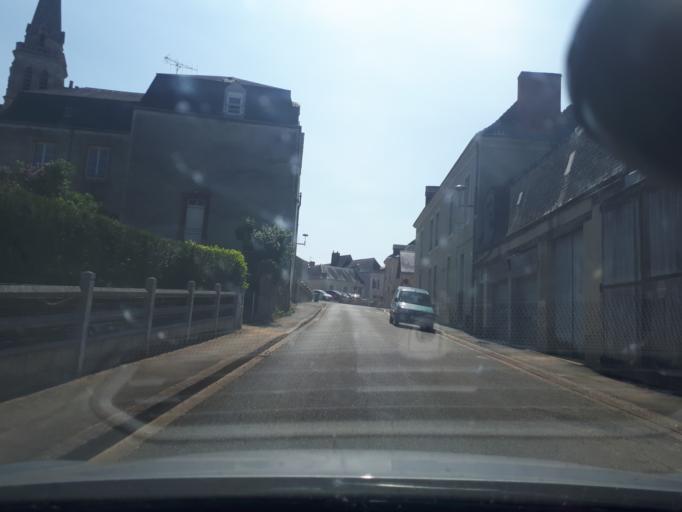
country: FR
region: Pays de la Loire
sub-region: Departement de la Sarthe
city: Montfort-le-Gesnois
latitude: 48.0495
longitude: 0.4023
